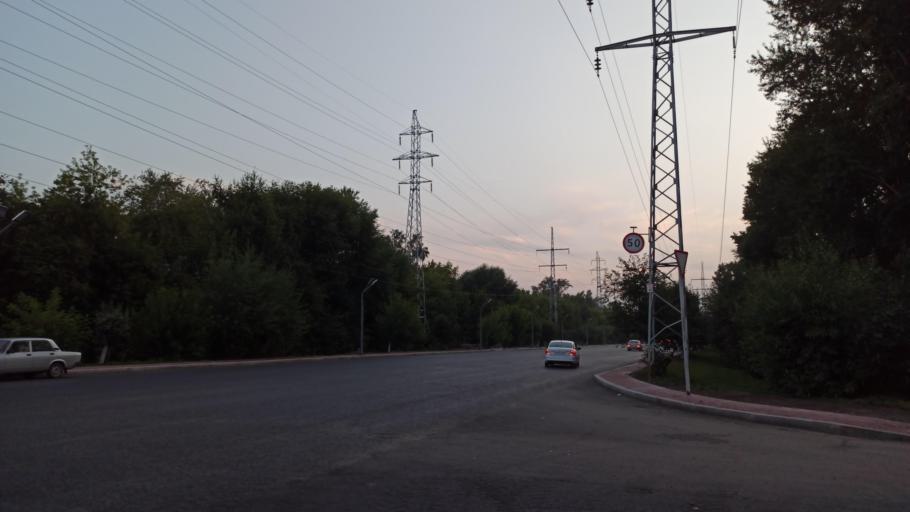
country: RU
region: Tomsk
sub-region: Tomskiy Rayon
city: Tomsk
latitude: 56.4553
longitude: 84.9677
